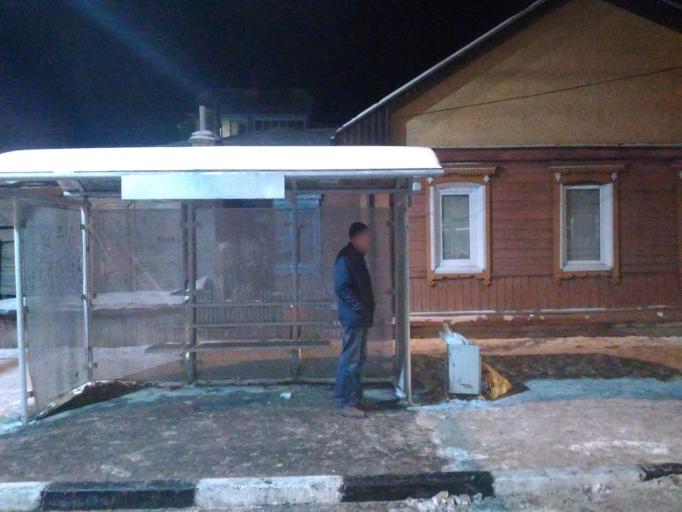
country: RU
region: Ulyanovsk
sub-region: Ulyanovskiy Rayon
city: Ulyanovsk
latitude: 54.3315
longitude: 48.4009
